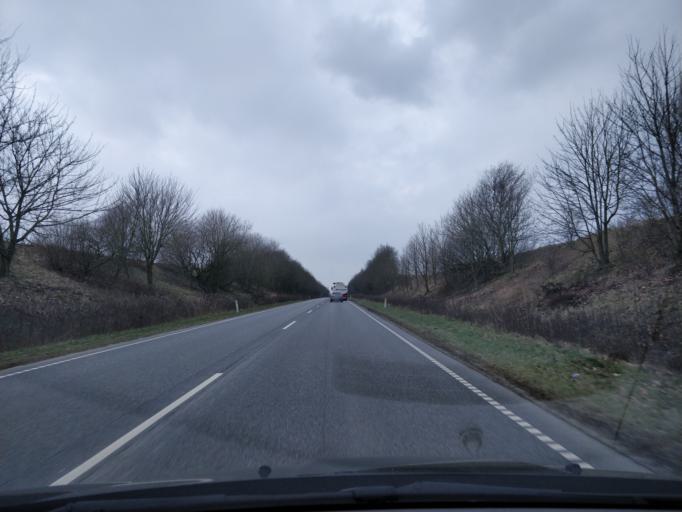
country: DK
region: South Denmark
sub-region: Vejle Kommune
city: Borkop
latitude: 55.6576
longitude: 9.6278
